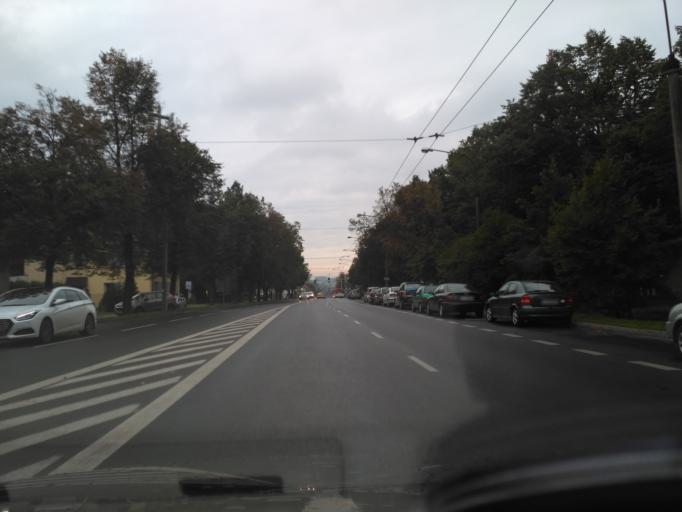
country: PL
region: Lublin Voivodeship
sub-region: Powiat lubelski
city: Lublin
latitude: 51.2321
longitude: 22.5891
